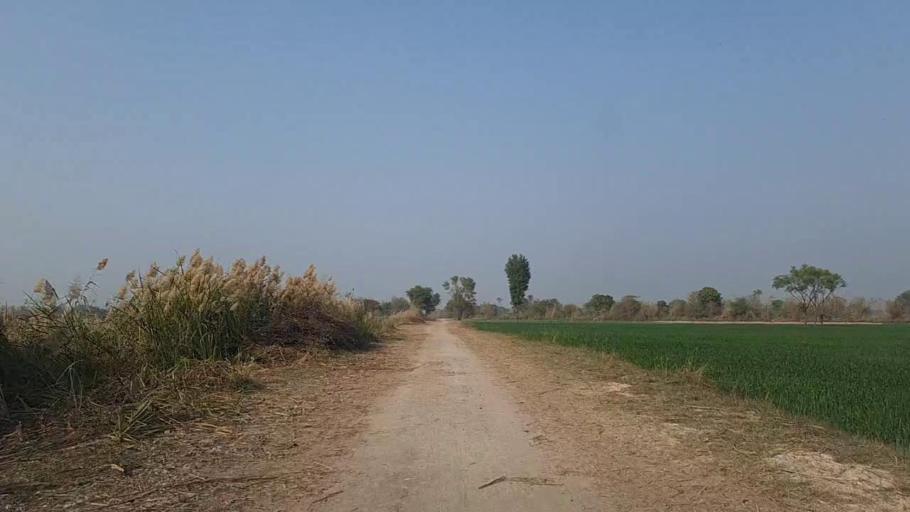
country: PK
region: Sindh
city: Nawabshah
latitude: 26.3518
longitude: 68.4741
